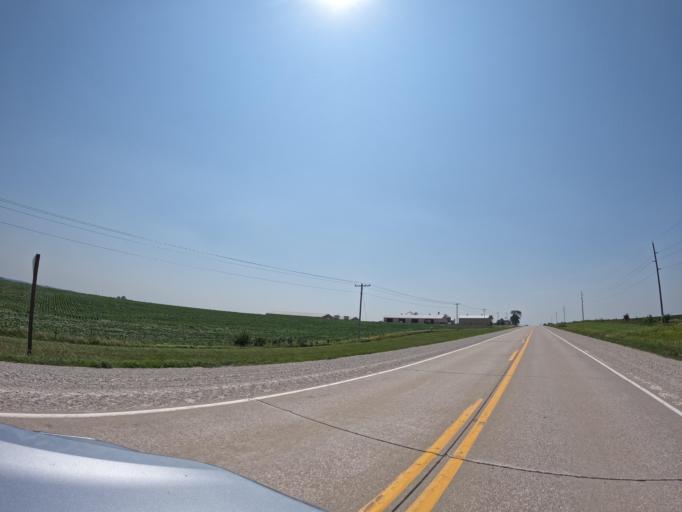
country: US
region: Iowa
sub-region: Keokuk County
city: Sigourney
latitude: 41.3368
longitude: -92.2476
